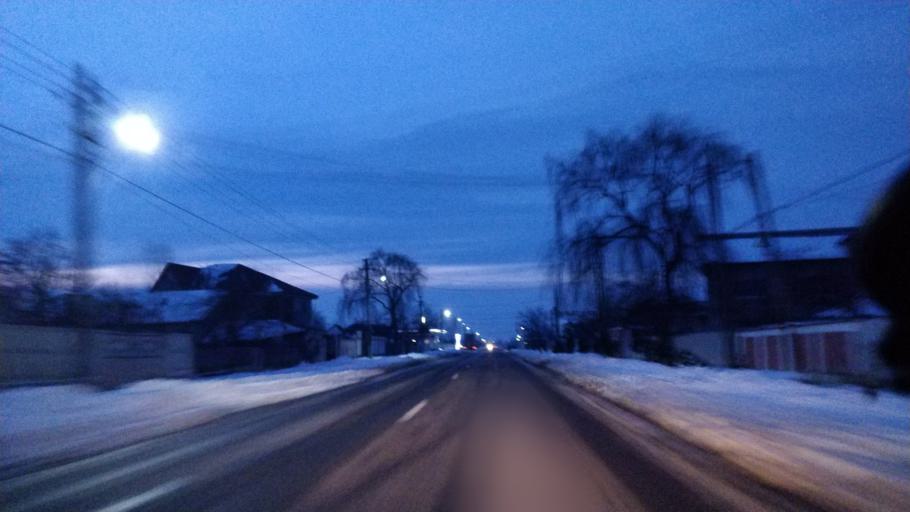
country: RO
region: Vrancea
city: Vulturu de Sus
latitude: 45.6224
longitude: 27.4042
